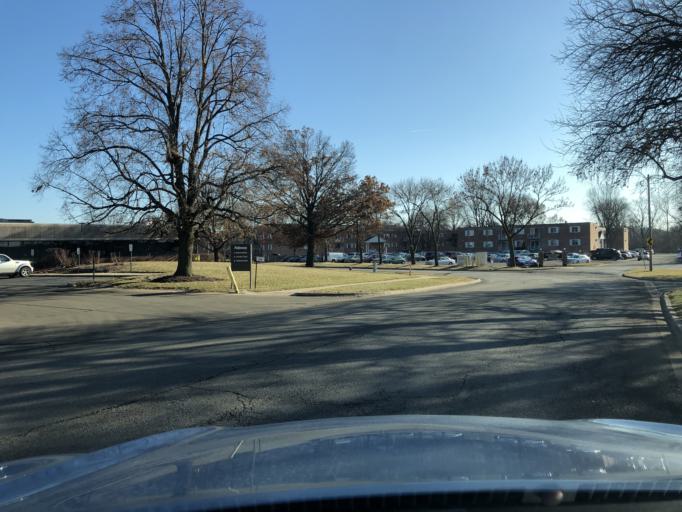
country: US
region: Illinois
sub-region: DuPage County
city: Roselle
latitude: 41.9883
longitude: -88.0462
